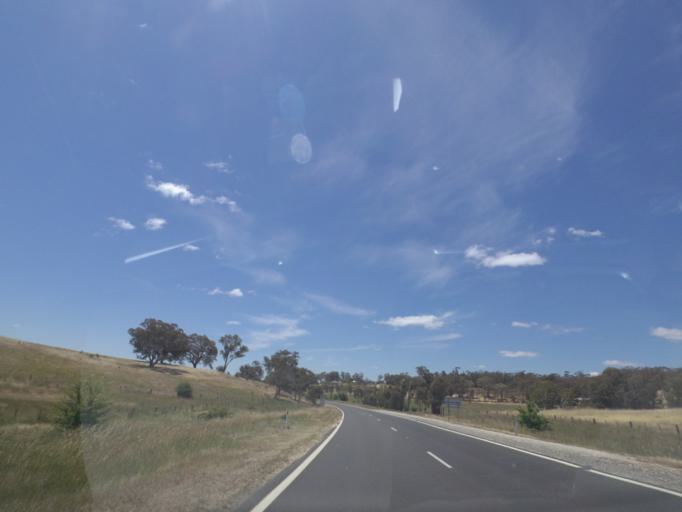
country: AU
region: Victoria
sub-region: Mount Alexander
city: Castlemaine
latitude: -37.1607
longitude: 144.1576
